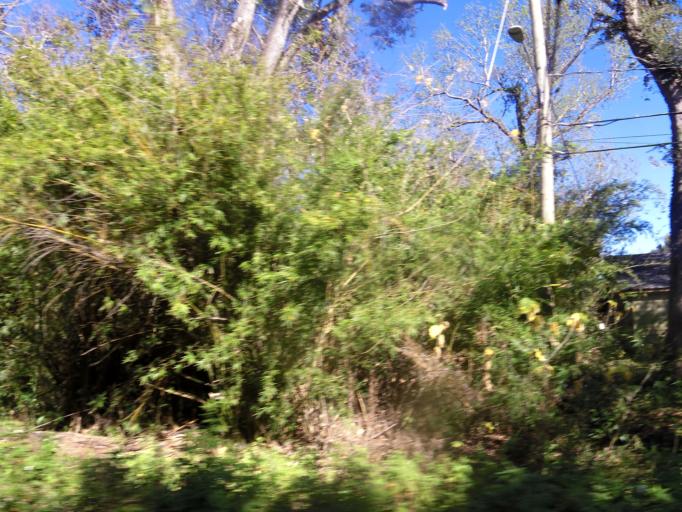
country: US
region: Florida
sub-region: Duval County
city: Jacksonville
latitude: 30.2819
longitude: -81.6482
